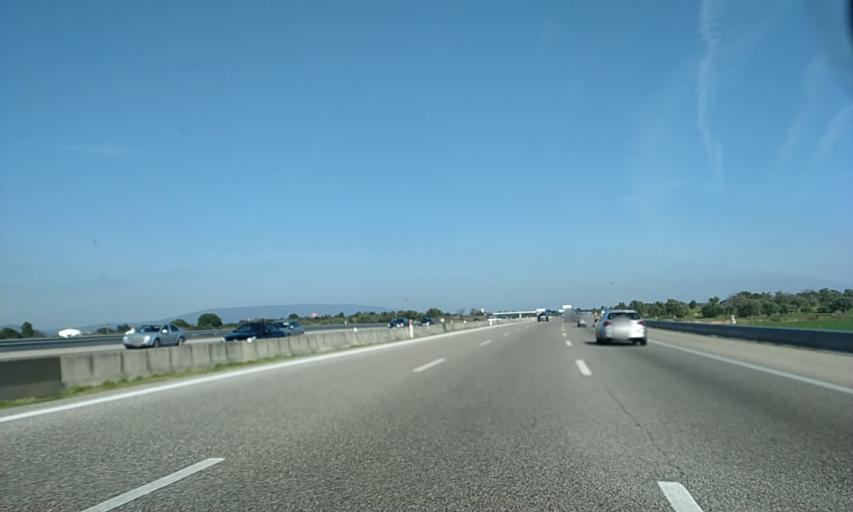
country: PT
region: Santarem
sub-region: Alcanena
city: Alcanena
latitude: 39.4129
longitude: -8.6355
